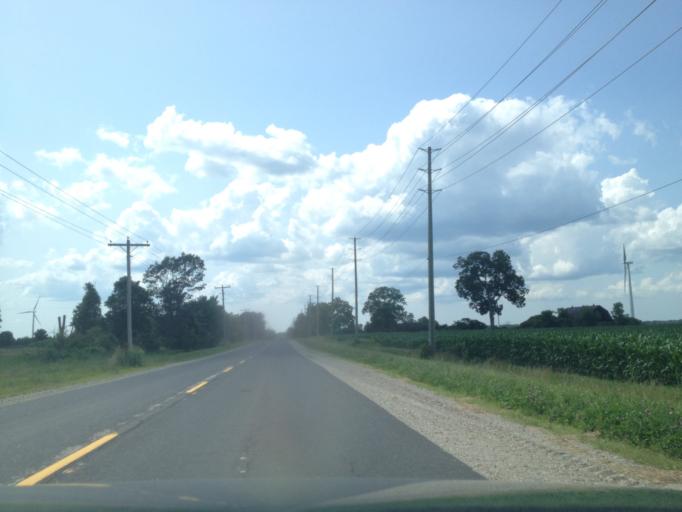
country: CA
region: Ontario
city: Aylmer
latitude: 42.6661
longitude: -80.8284
